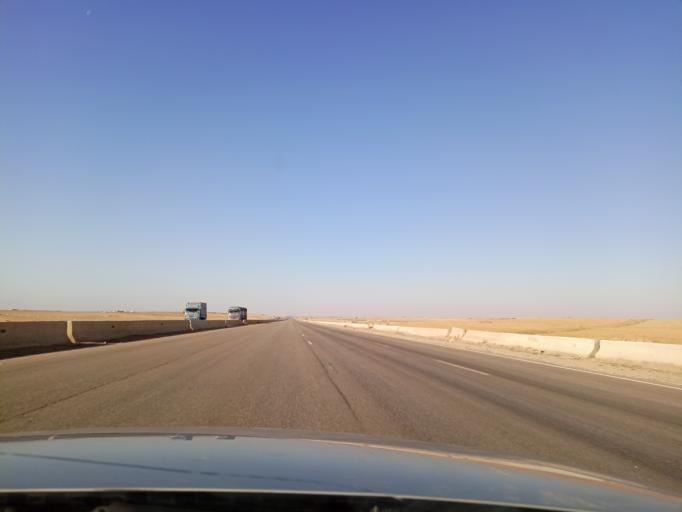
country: EG
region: Muhafazat al Fayyum
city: Tamiyah
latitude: 29.6118
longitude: 30.9216
